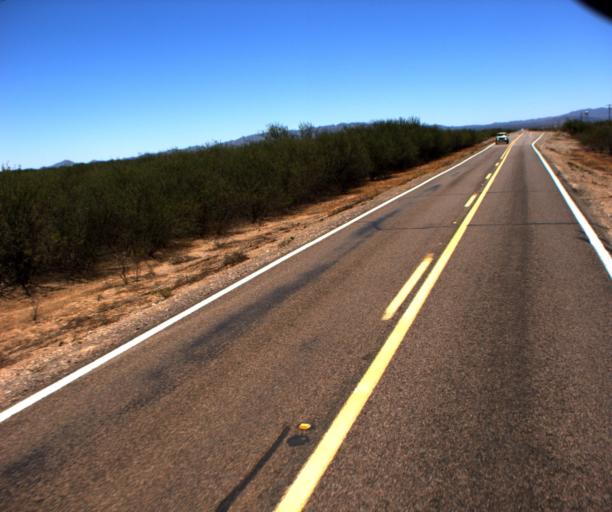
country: US
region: Arizona
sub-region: Pima County
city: Ajo
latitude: 32.1913
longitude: -112.4204
